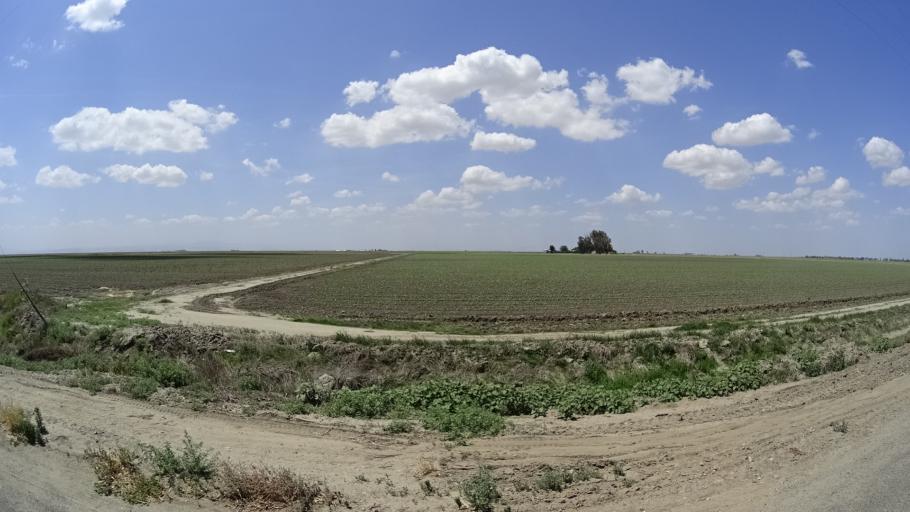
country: US
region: California
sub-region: Kings County
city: Stratford
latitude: 36.1602
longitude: -119.8160
